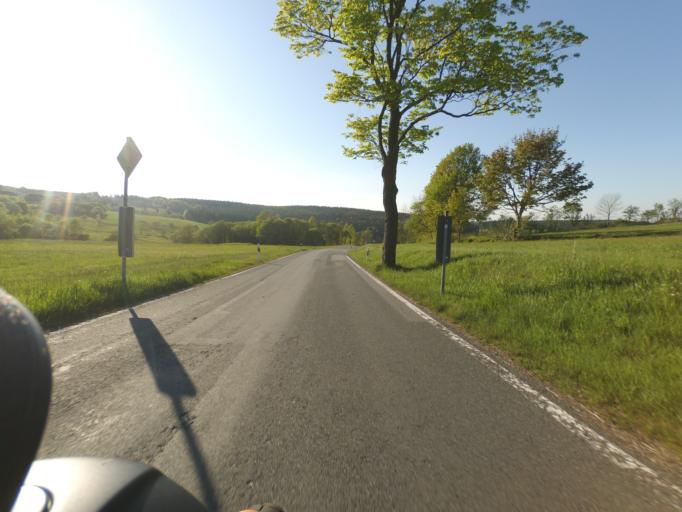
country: DE
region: Saxony
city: Altenberg
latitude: 50.7693
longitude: 13.7553
